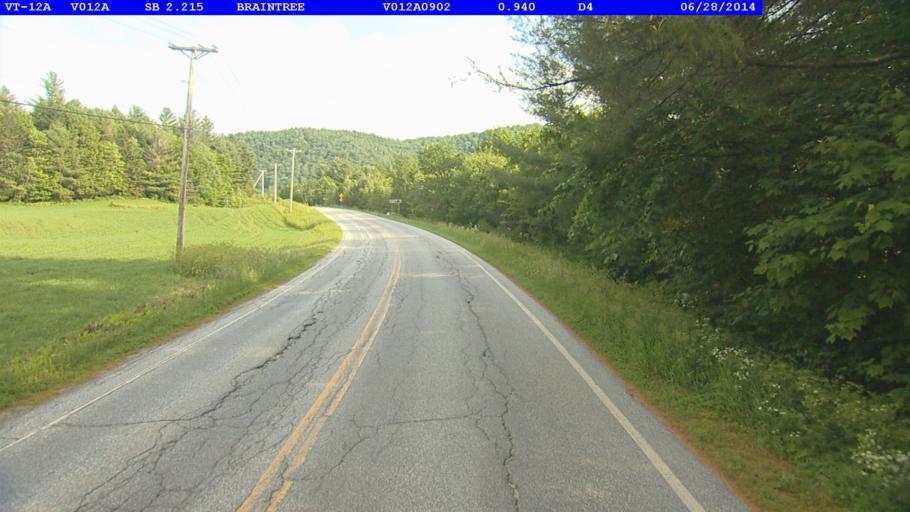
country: US
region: Vermont
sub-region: Orange County
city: Randolph
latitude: 43.9360
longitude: -72.7037
